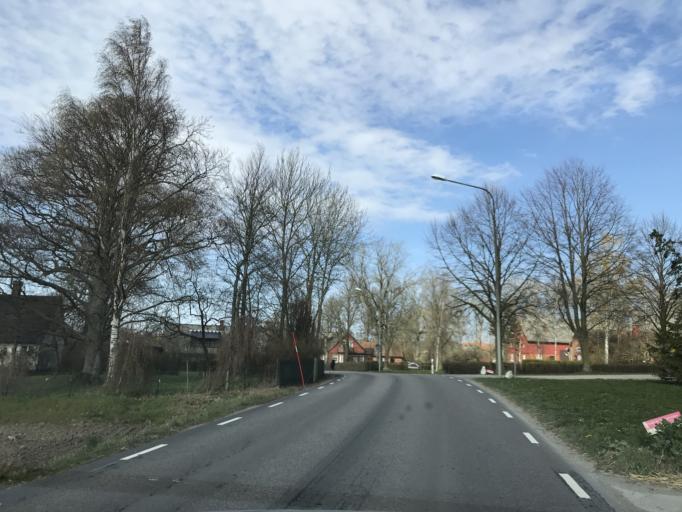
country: SE
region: Skane
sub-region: Lunds Kommun
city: Genarp
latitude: 55.6461
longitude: 13.3481
